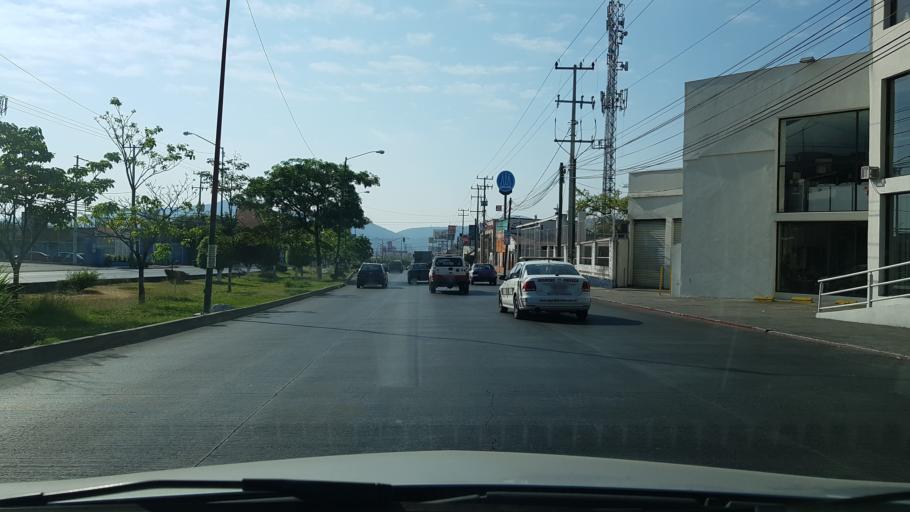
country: MX
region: Morelos
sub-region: Jiutepec
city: Jiutepec
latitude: 18.9018
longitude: -99.1737
